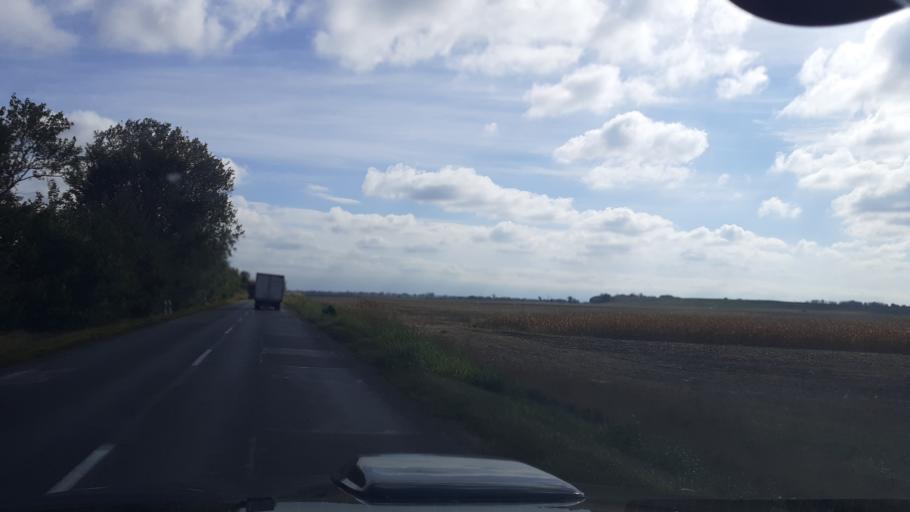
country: HU
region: Bacs-Kiskun
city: Solt
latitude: 46.7977
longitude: 19.0513
